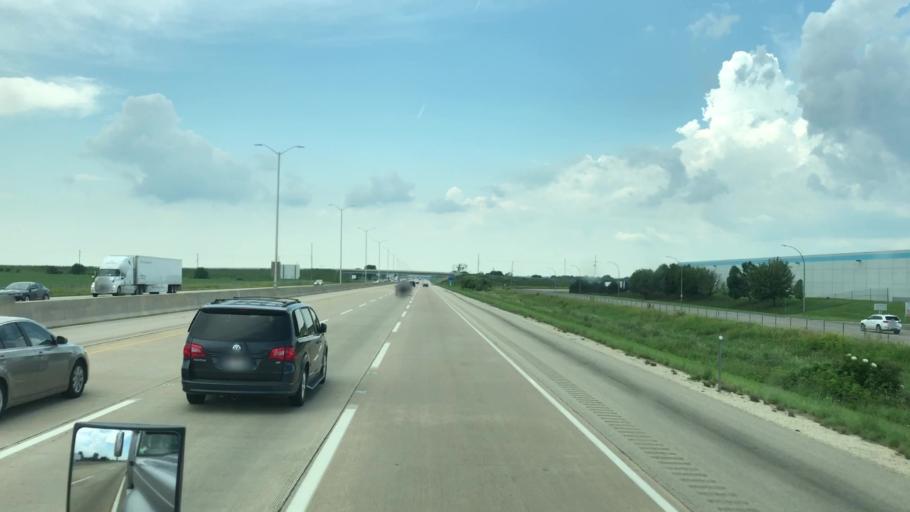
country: US
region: Illinois
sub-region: Boone County
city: Belvidere
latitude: 42.2334
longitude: -88.8746
